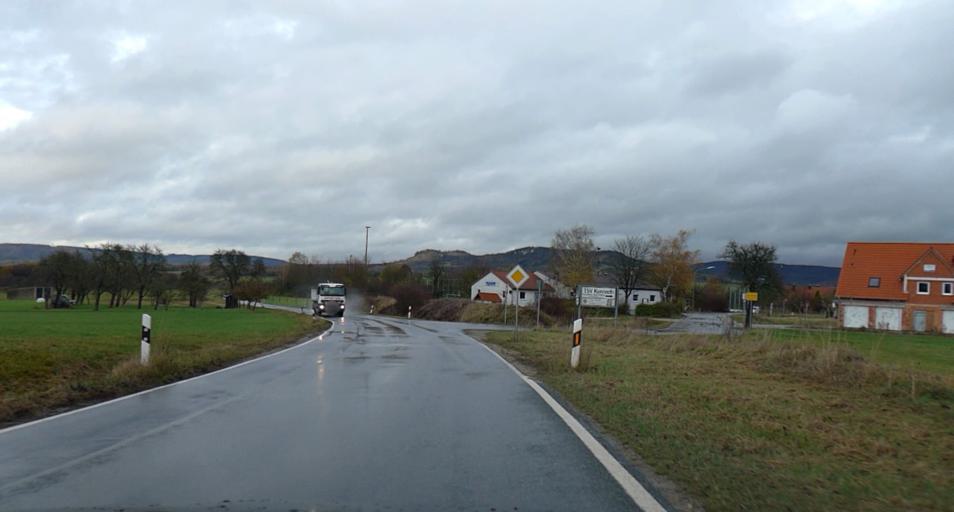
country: DE
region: Bavaria
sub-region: Upper Franconia
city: Kunreuth
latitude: 49.6791
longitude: 11.1357
